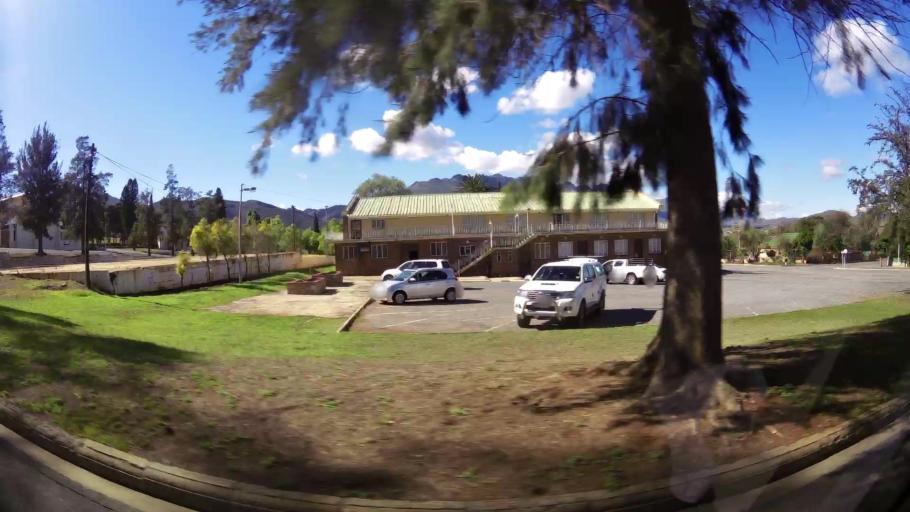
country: ZA
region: Western Cape
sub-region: Cape Winelands District Municipality
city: Ashton
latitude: -33.8319
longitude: 20.0551
